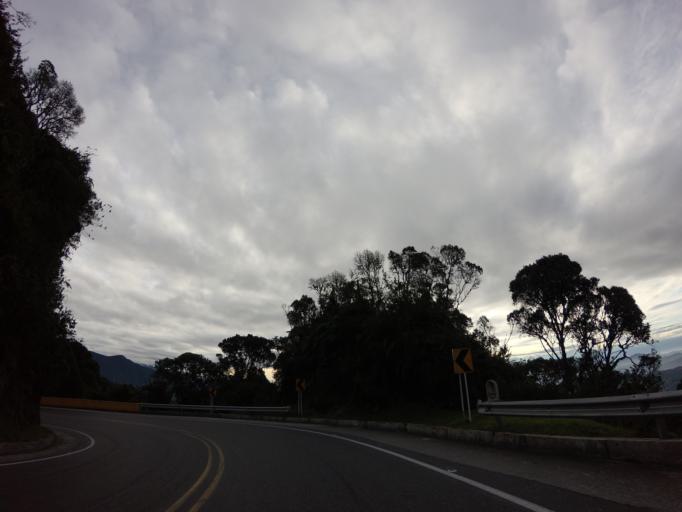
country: CO
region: Tolima
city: Herveo
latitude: 5.0949
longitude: -75.2774
